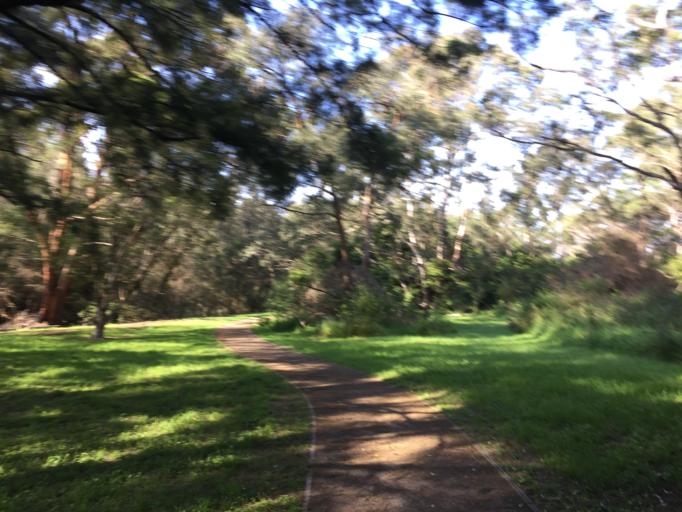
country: AU
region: New South Wales
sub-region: Ryde
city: East Ryde
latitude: -33.8144
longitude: 151.1342
